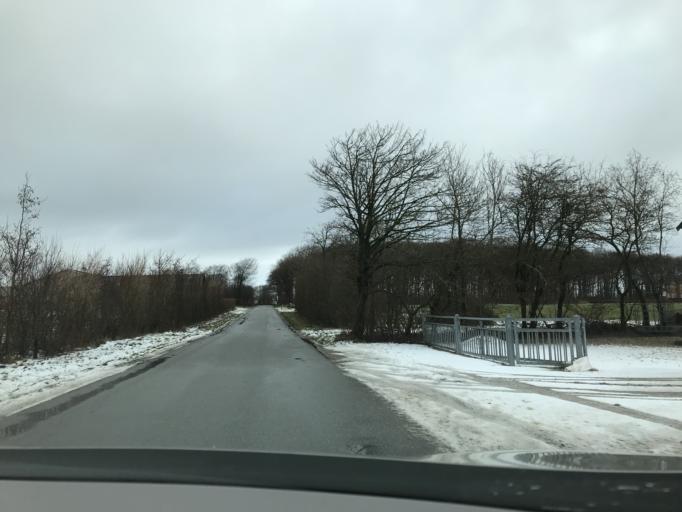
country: DK
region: South Denmark
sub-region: Varde Kommune
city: Varde
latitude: 55.6574
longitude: 8.4177
